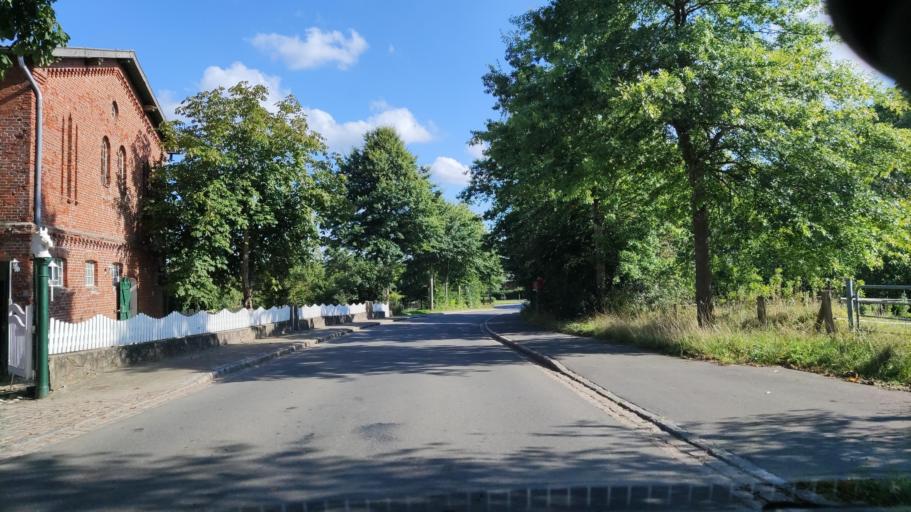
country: DE
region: Schleswig-Holstein
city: Oldenhutten
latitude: 54.1588
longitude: 9.7363
